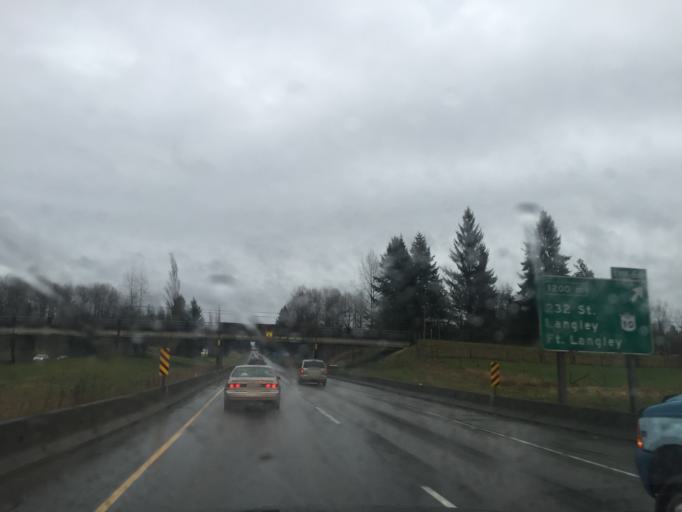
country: CA
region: British Columbia
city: Walnut Grove
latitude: 49.1446
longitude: -122.6028
